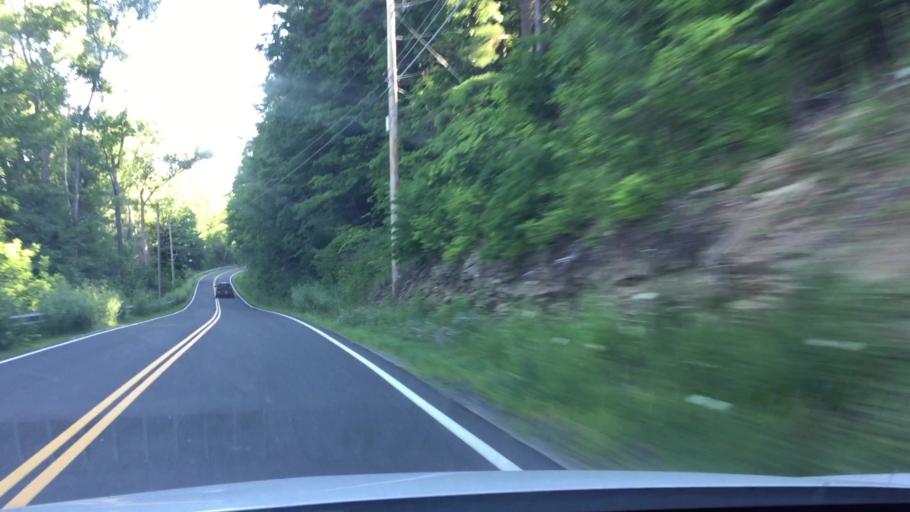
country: US
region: Massachusetts
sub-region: Berkshire County
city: Lee
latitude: 42.2782
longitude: -73.2392
